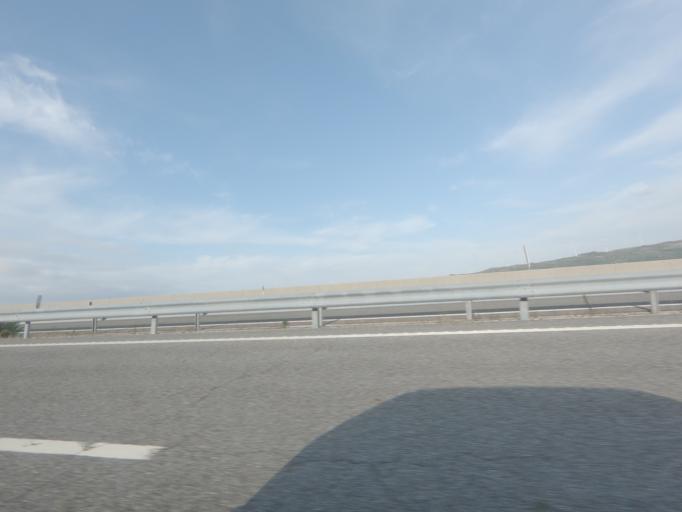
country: PT
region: Vila Real
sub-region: Vila Pouca de Aguiar
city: Vila Pouca de Aguiar
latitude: 41.4980
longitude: -7.6560
